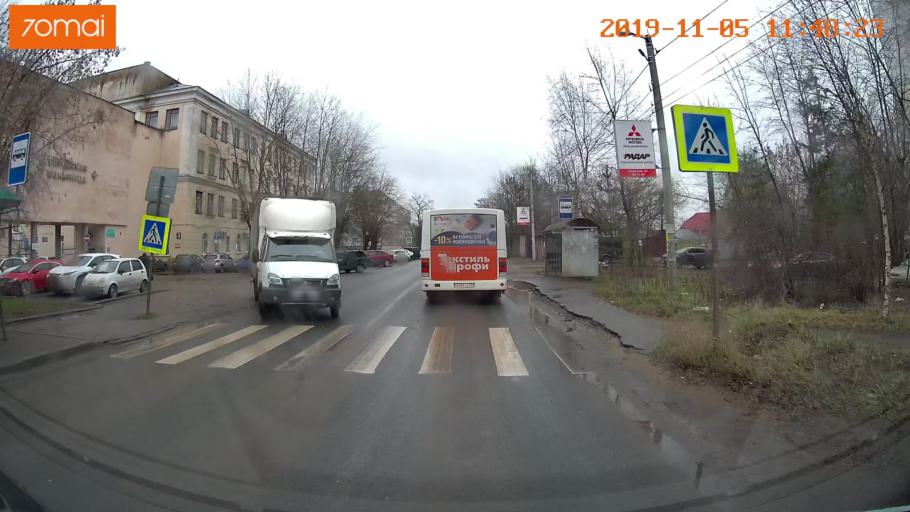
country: RU
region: Ivanovo
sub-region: Gorod Ivanovo
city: Ivanovo
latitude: 57.0087
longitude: 40.9972
